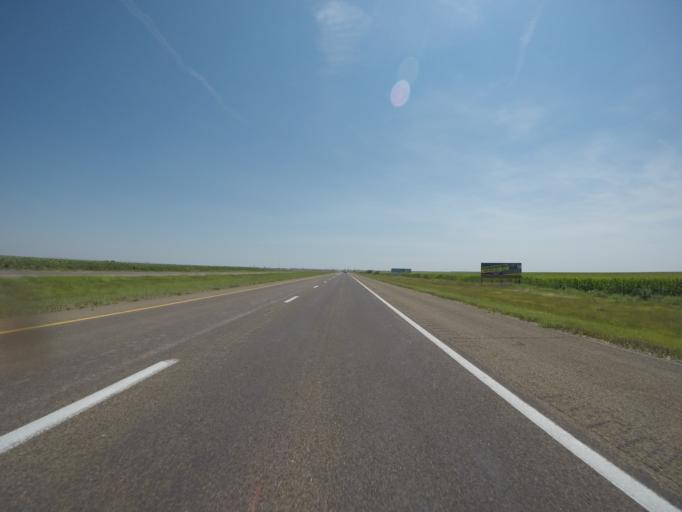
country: US
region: Kansas
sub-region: Thomas County
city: Colby
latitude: 39.3648
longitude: -101.1011
